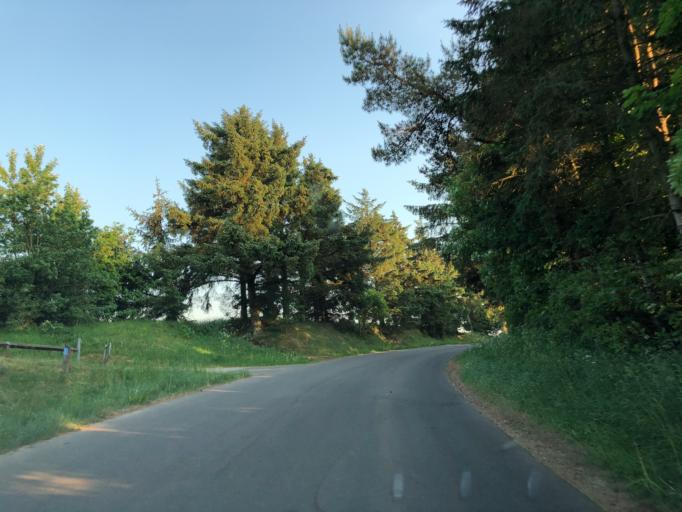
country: DK
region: Central Jutland
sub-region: Struer Kommune
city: Struer
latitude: 56.4300
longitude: 8.5054
